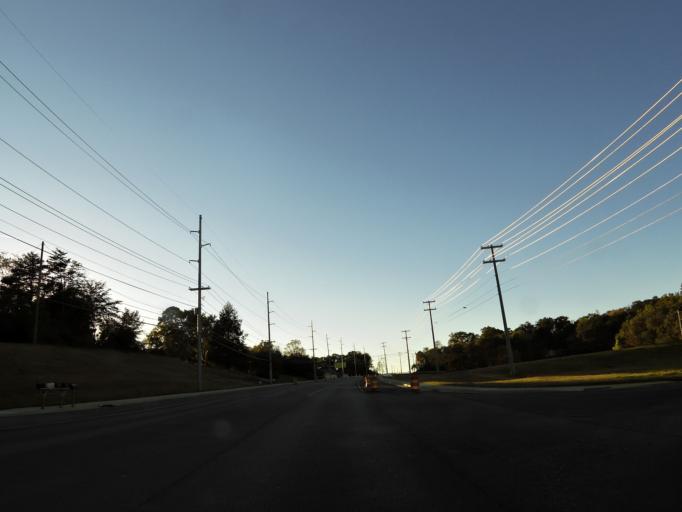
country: US
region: Tennessee
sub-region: Knox County
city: Knoxville
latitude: 35.9844
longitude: -84.0292
